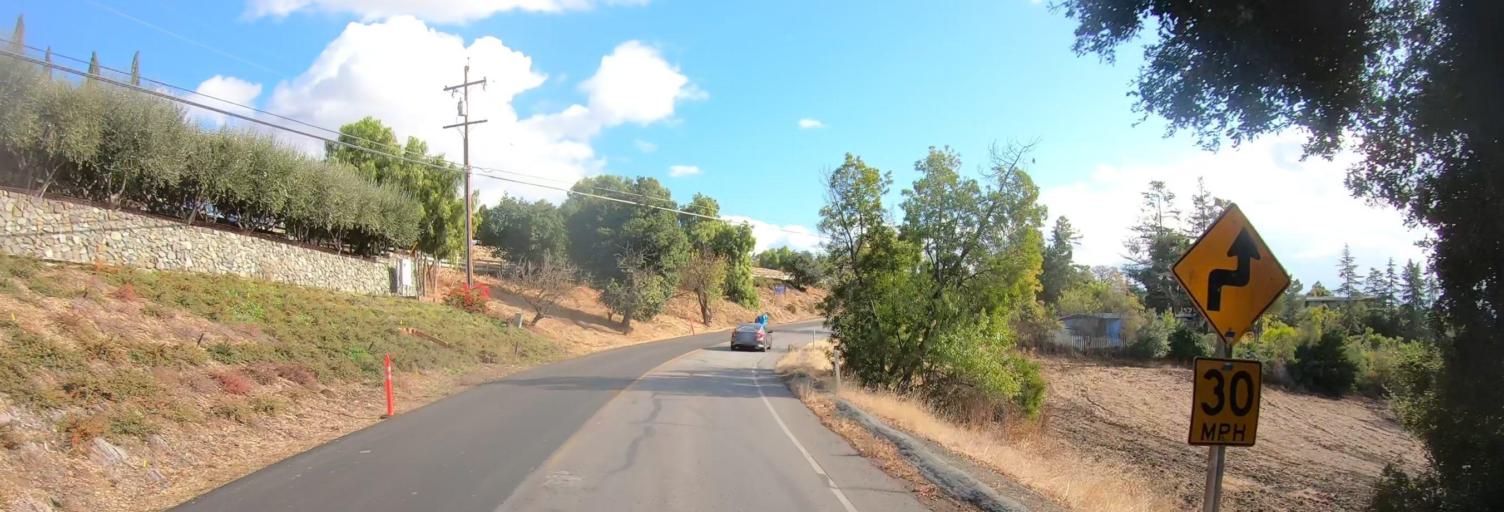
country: US
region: California
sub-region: Santa Clara County
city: East Foothills
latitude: 37.3835
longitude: -121.8150
